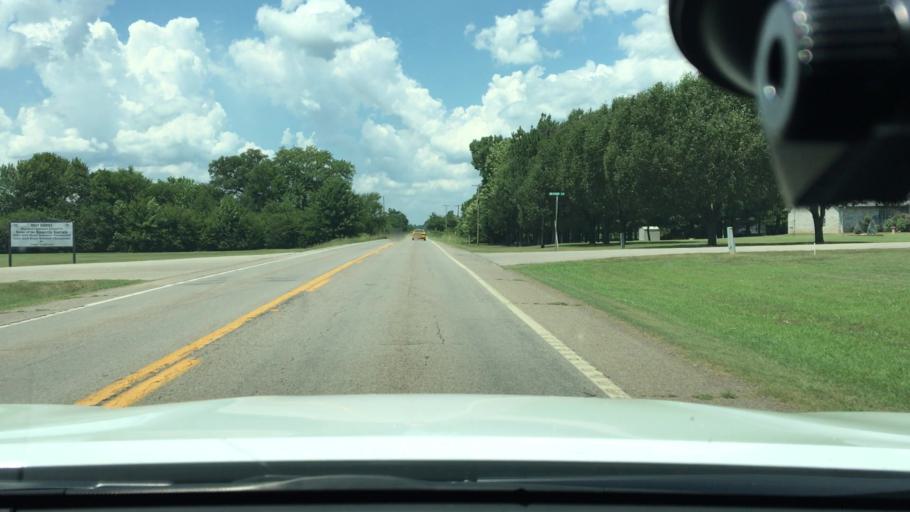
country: US
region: Arkansas
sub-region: Logan County
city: Booneville
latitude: 35.1476
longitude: -93.8529
